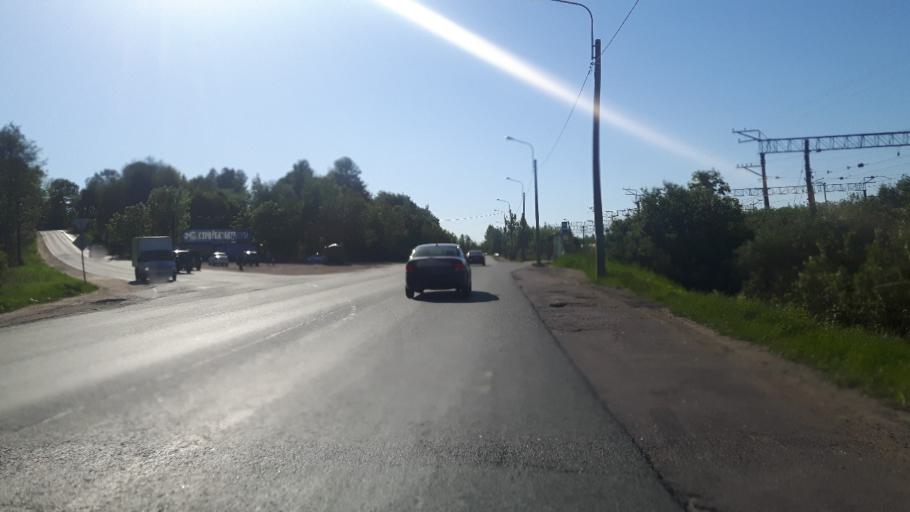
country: RU
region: St.-Petersburg
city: Bol'shaya Izhora
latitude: 59.9275
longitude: 29.6576
